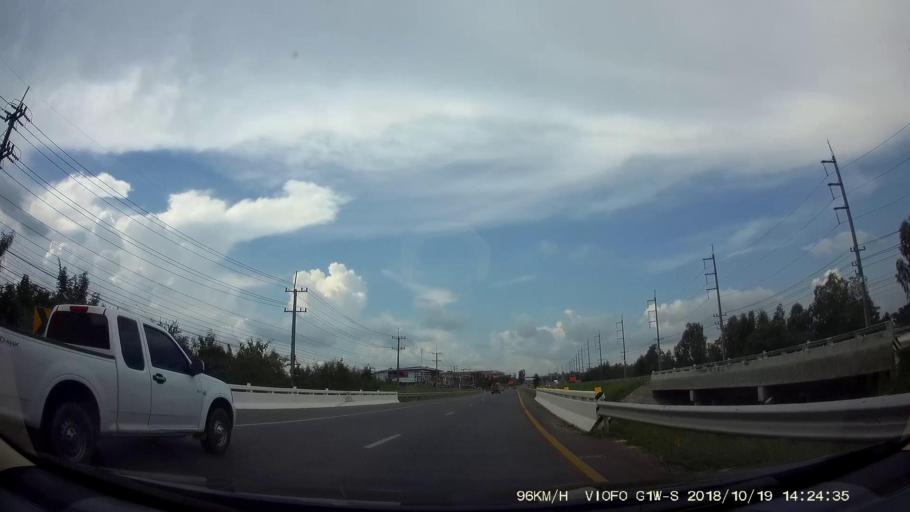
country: TH
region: Chaiyaphum
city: Kaeng Khro
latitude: 16.0824
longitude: 102.2714
